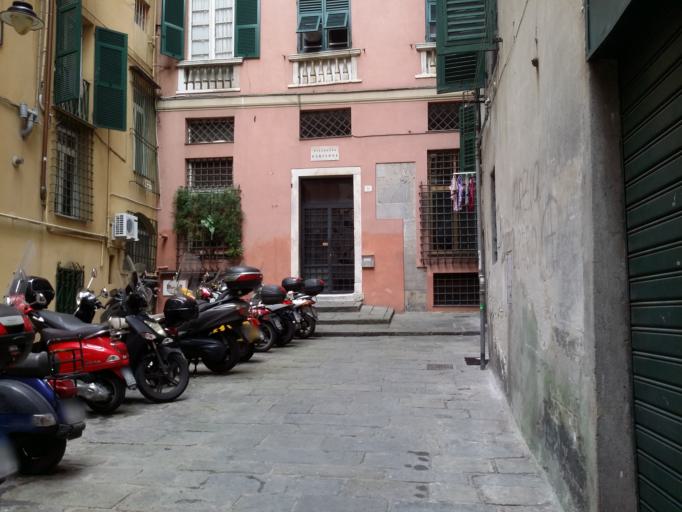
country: IT
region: Liguria
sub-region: Provincia di Genova
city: San Teodoro
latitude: 44.4068
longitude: 8.9286
